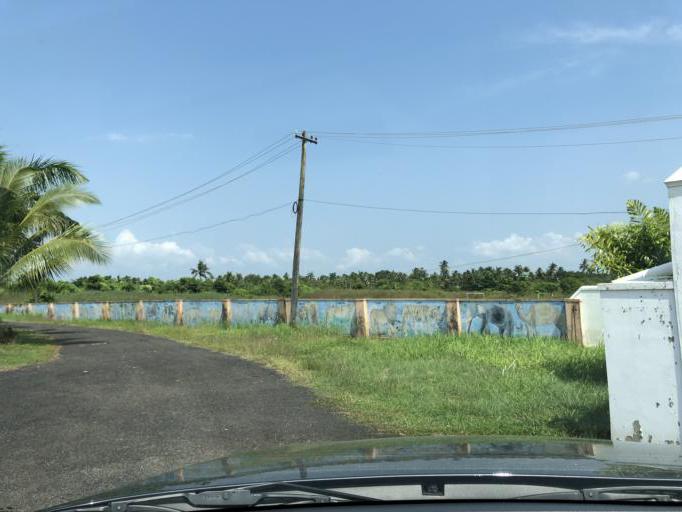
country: IN
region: Kerala
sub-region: Ernakulam
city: Cochin
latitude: 9.9961
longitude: 76.2332
